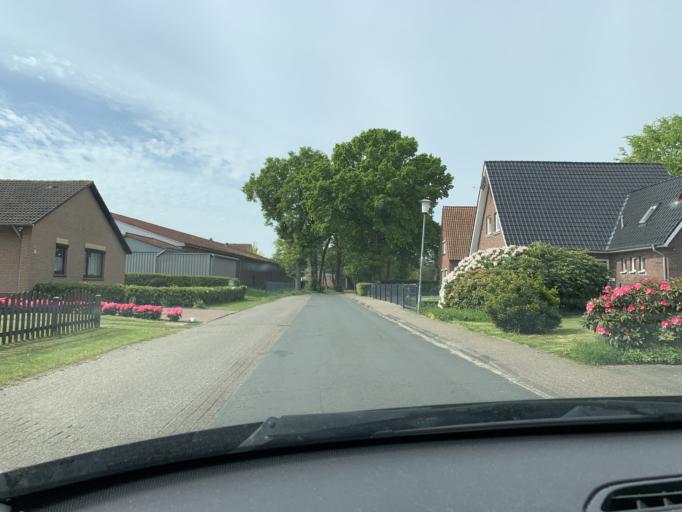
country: DE
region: Lower Saxony
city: Apen
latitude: 53.2244
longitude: 7.8125
